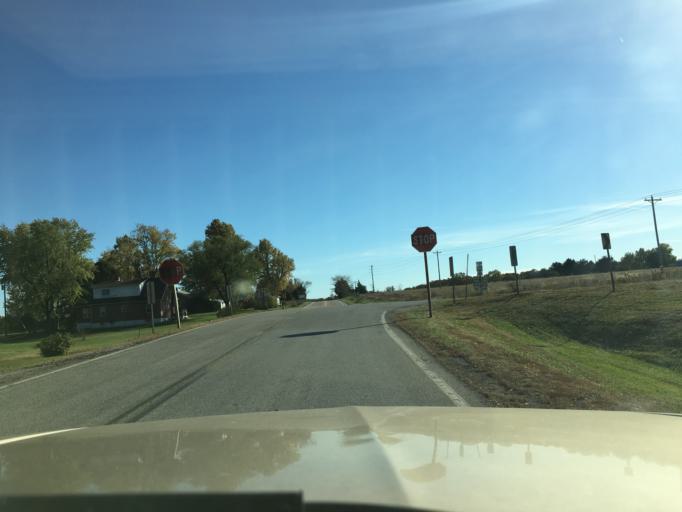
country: US
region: Missouri
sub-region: Gasconade County
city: Owensville
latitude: 38.4677
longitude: -91.4650
